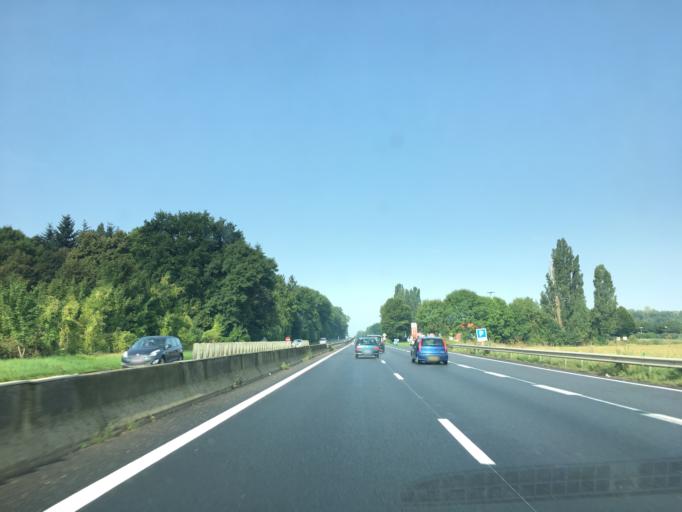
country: FR
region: Ile-de-France
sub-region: Departement de Seine-et-Marne
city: Ozoir-la-Ferriere
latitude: 48.7662
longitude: 2.6529
